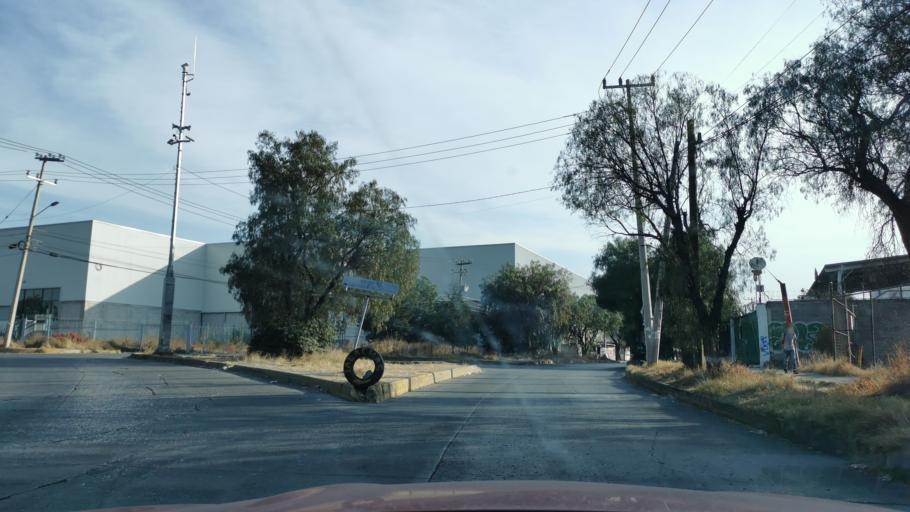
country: MX
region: Mexico
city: Cuautitlan
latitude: 19.6693
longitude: -99.2030
